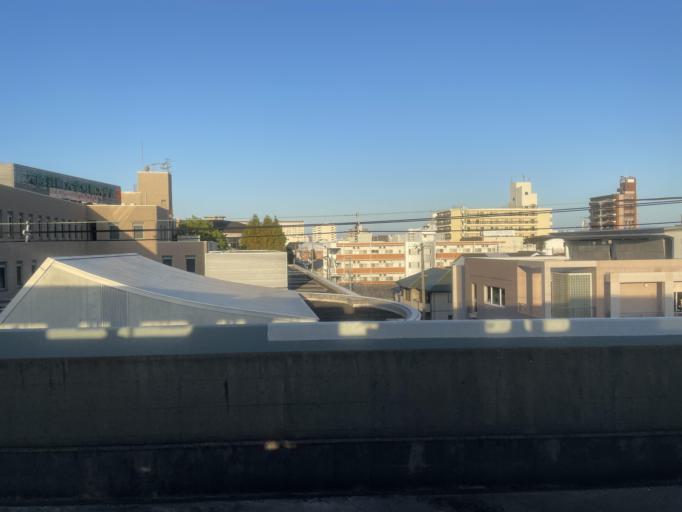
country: JP
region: Osaka
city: Matsubara
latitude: 34.6083
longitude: 135.5332
